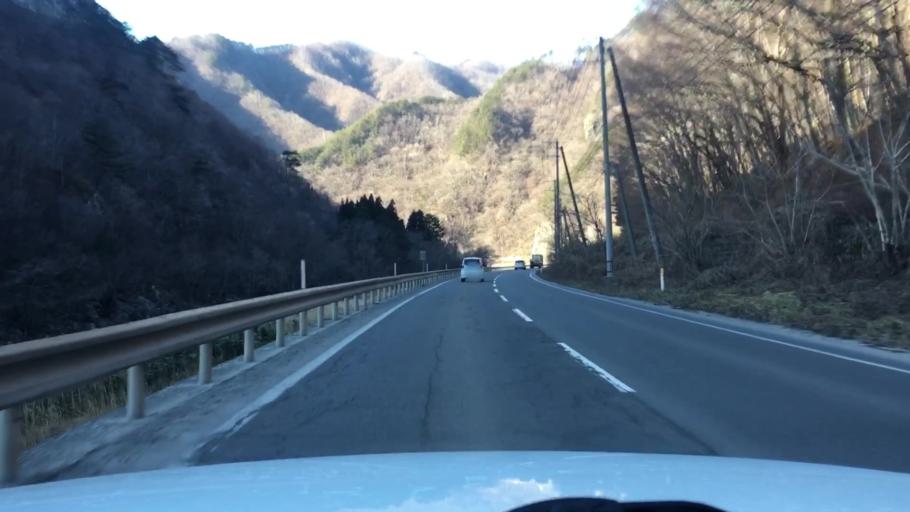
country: JP
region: Iwate
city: Miyako
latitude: 39.6074
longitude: 141.7814
